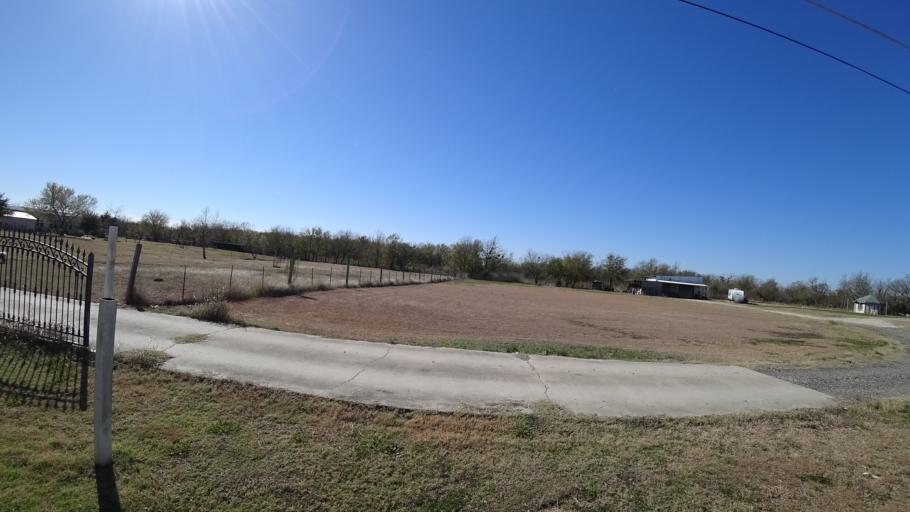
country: US
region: Texas
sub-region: Travis County
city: Garfield
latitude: 30.0987
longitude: -97.6213
